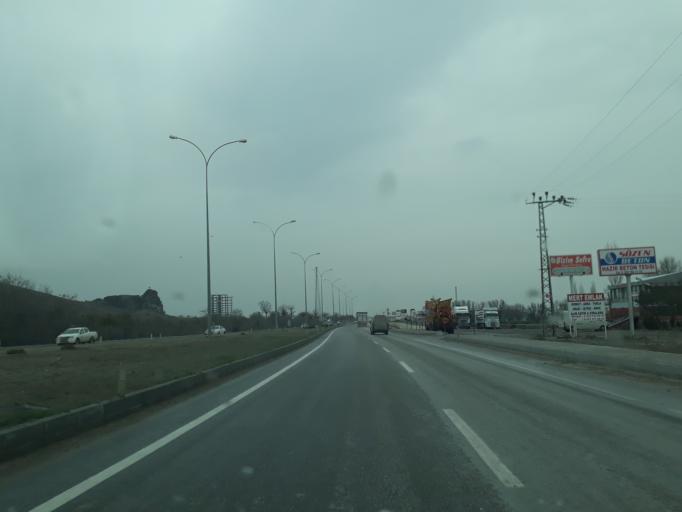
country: TR
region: Konya
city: Karapinar
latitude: 37.7151
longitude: 33.5814
